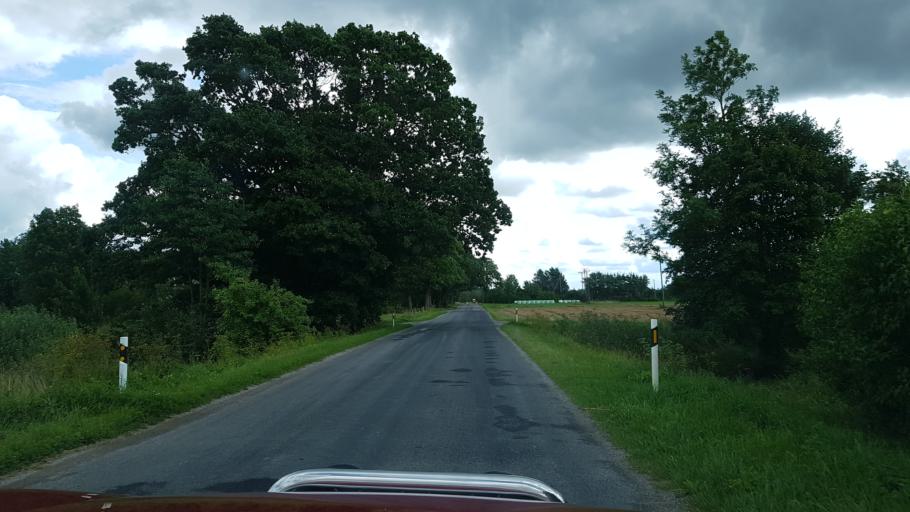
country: EE
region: Laeaene
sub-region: Lihula vald
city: Lihula
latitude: 58.7122
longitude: 24.0067
